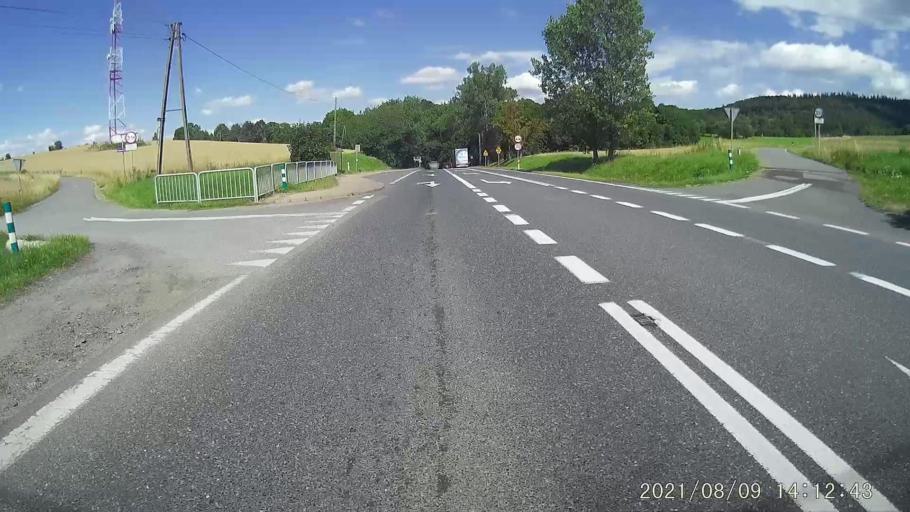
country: PL
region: Lower Silesian Voivodeship
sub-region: Powiat zabkowicki
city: Bardo
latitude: 50.4792
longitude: 16.7091
